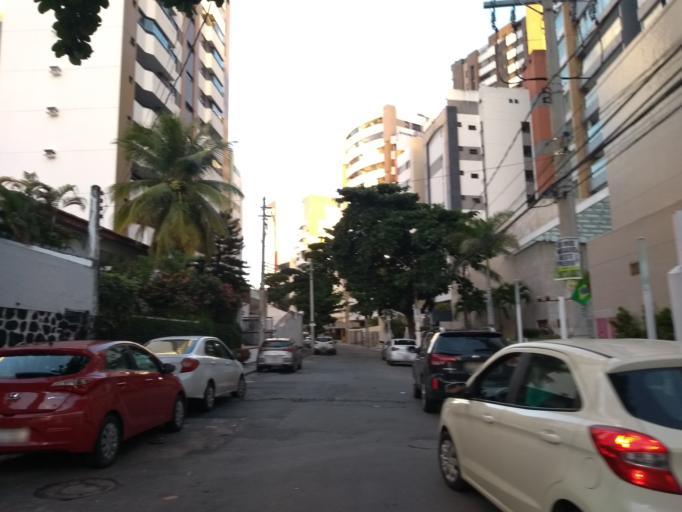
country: BR
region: Bahia
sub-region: Salvador
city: Salvador
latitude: -12.9974
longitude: -38.4615
